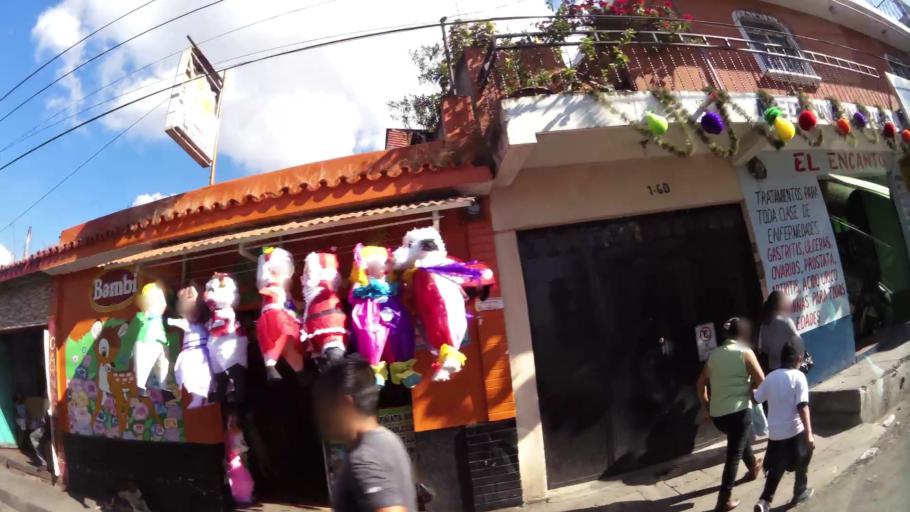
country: GT
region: Guatemala
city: Villa Nueva
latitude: 14.5242
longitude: -90.5903
